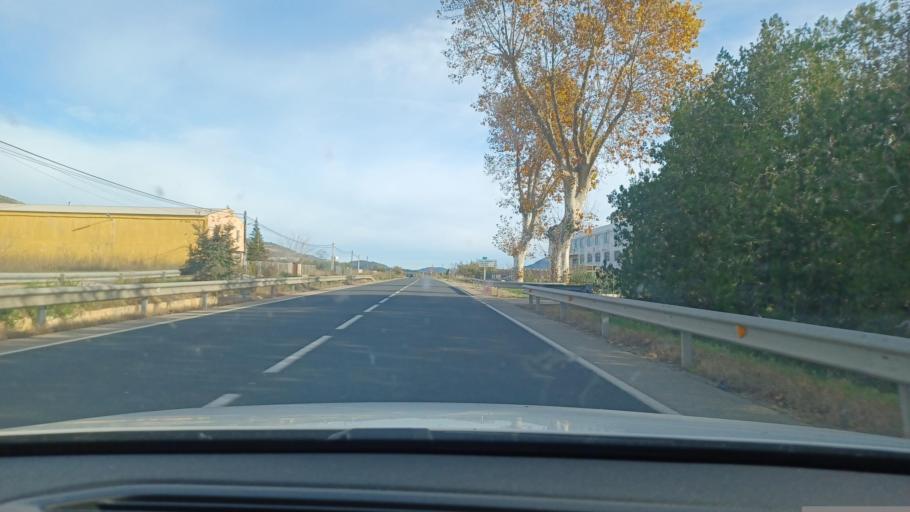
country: ES
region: Catalonia
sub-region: Provincia de Tarragona
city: Ulldecona
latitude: 40.6049
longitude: 0.4564
